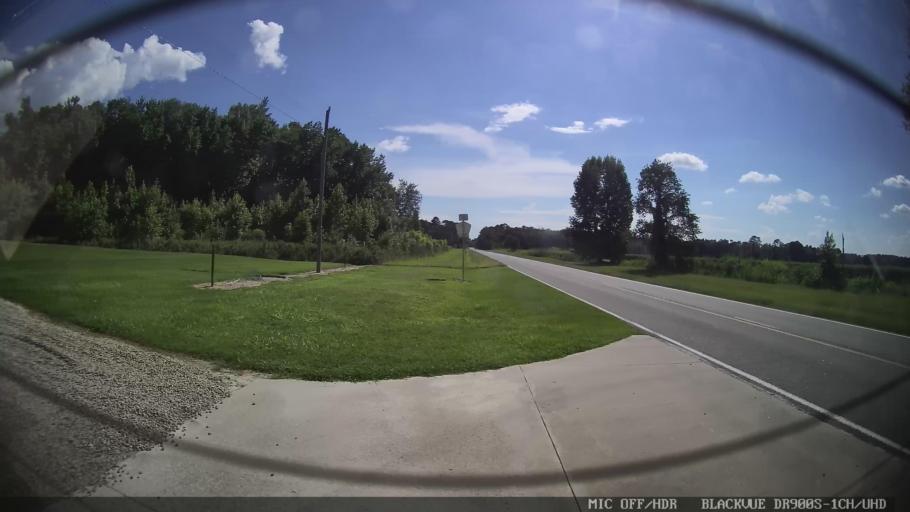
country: US
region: Georgia
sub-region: Echols County
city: Statenville
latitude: 30.5673
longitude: -83.1604
